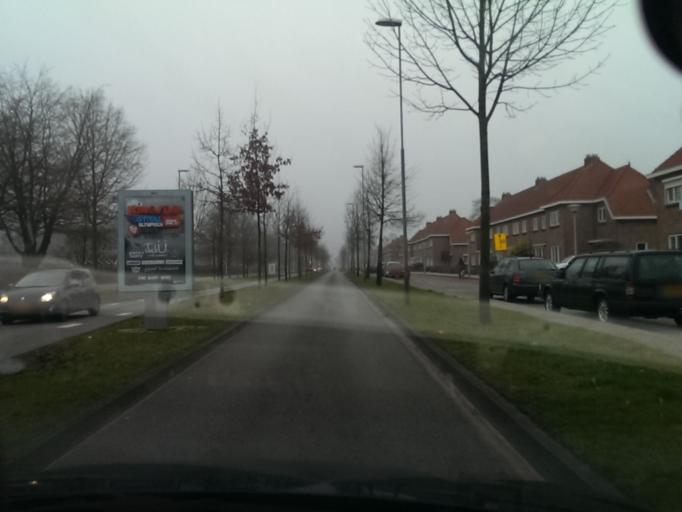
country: NL
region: North Brabant
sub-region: Gemeente Eindhoven
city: Eindhoven
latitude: 51.4590
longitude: 5.4573
